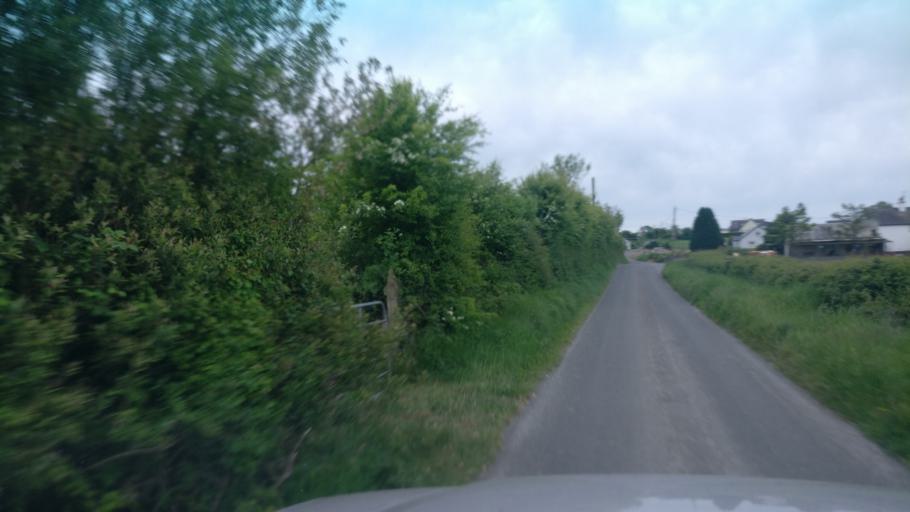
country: IE
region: Connaught
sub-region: County Galway
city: Portumna
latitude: 53.1398
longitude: -8.2906
